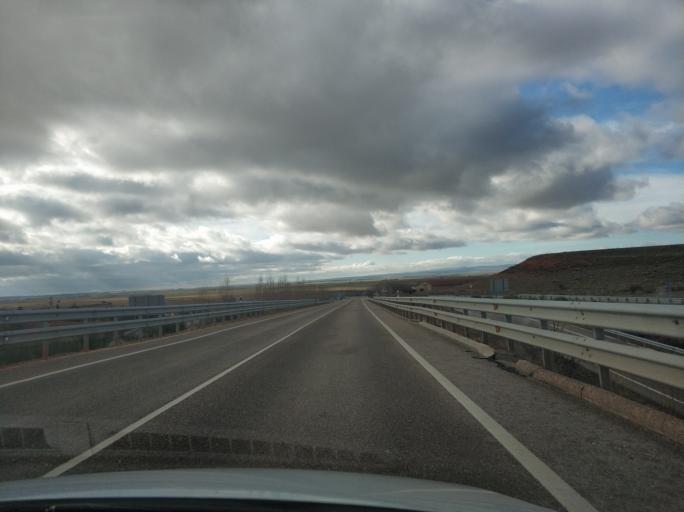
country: ES
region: Castille and Leon
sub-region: Provincia de Segovia
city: Ayllon
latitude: 41.4301
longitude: -3.3759
